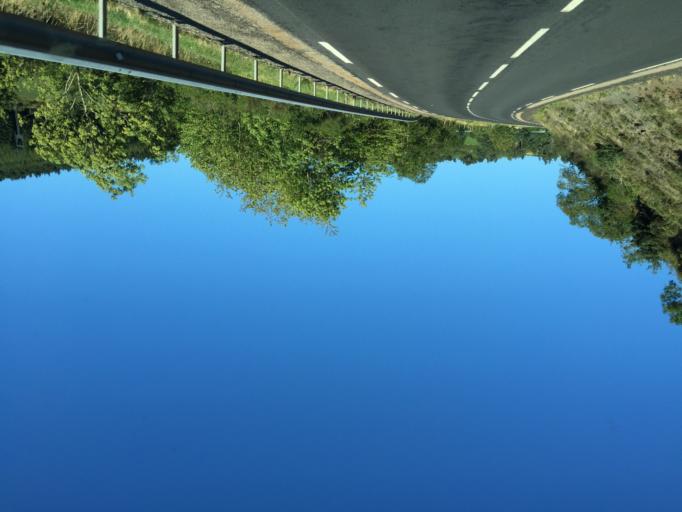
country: FR
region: Auvergne
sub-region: Departement de la Haute-Loire
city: Bains
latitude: 44.9869
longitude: 3.7033
